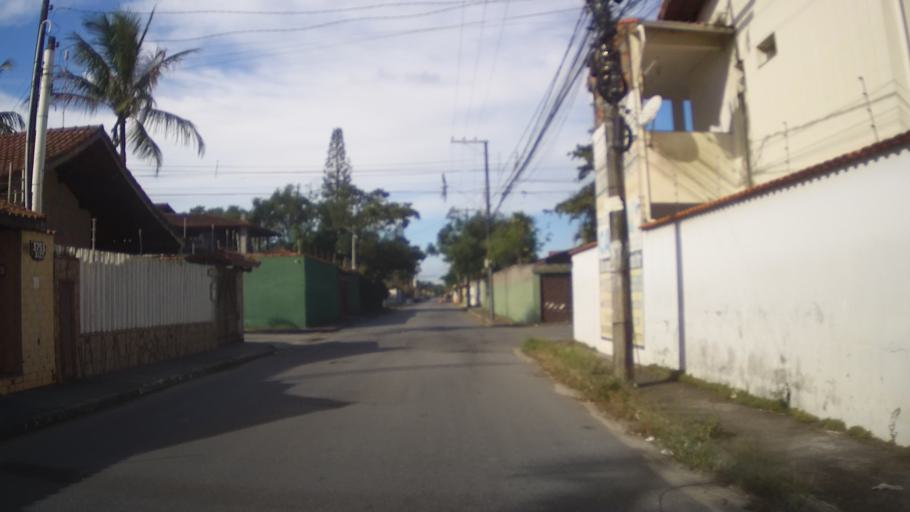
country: BR
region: Sao Paulo
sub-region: Itanhaem
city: Itanhaem
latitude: -24.1663
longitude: -46.7551
